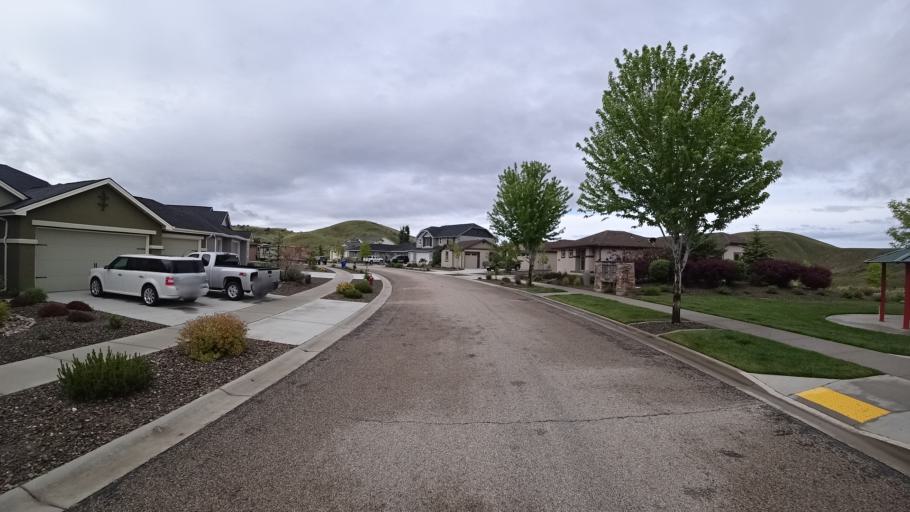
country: US
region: Idaho
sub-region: Ada County
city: Eagle
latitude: 43.7700
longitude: -116.2599
